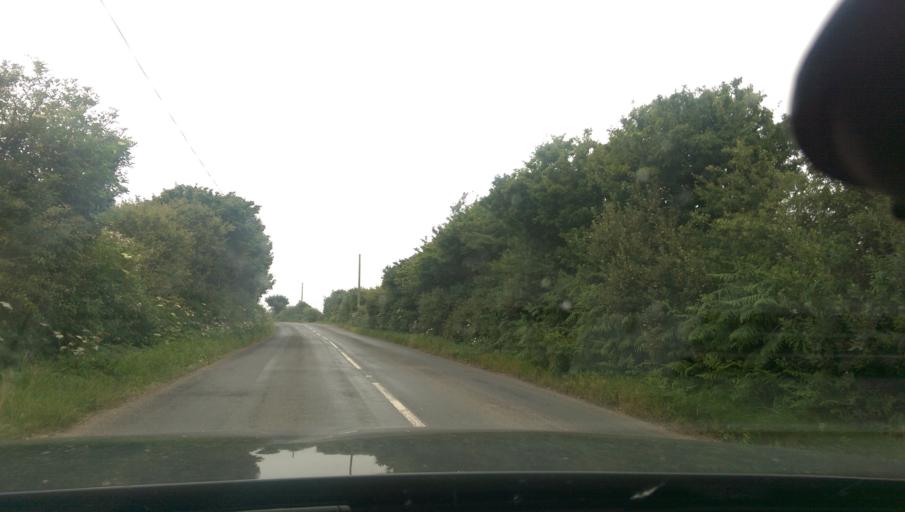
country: GB
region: England
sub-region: Cornwall
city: St. Buryan
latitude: 50.0911
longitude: -5.6291
